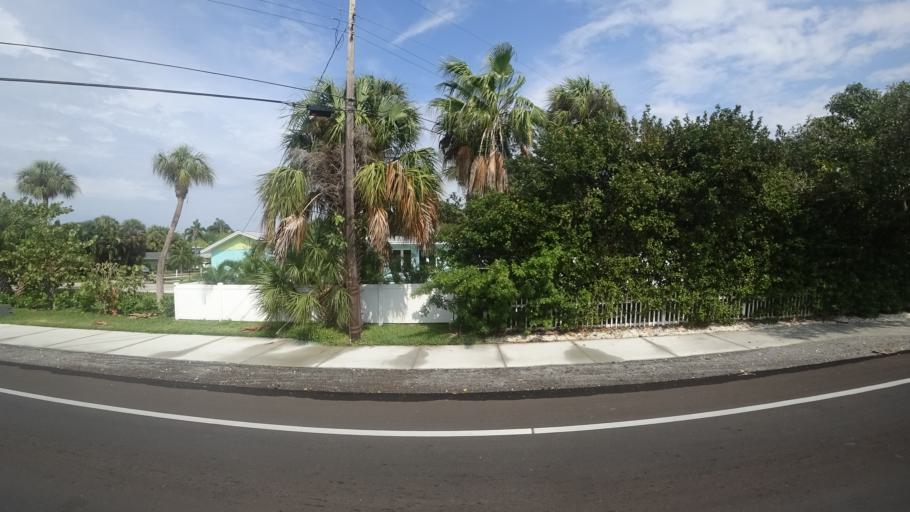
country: US
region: Florida
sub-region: Manatee County
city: Anna Maria
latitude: 27.5168
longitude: -82.7217
